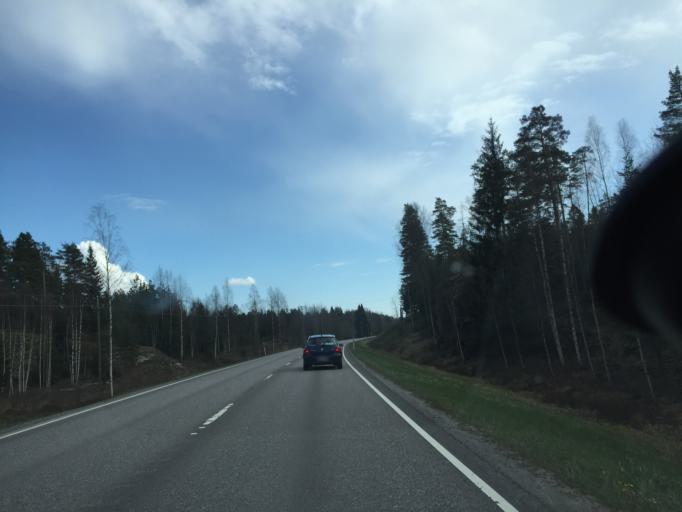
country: FI
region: Uusimaa
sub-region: Raaseporin
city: Ekenaes
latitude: 60.0134
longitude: 23.3941
